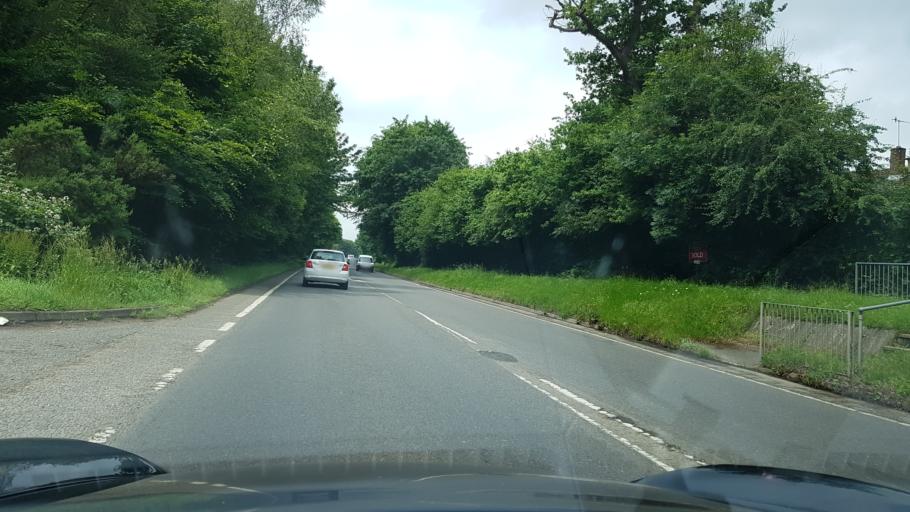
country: GB
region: England
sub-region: West Sussex
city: Copthorne
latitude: 51.1340
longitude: -0.1193
